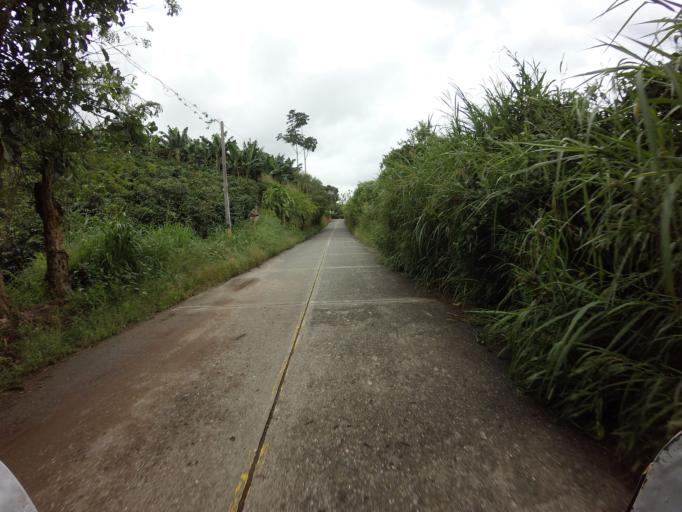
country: CO
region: Valle del Cauca
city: Ulloa
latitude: 4.7002
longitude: -75.7630
